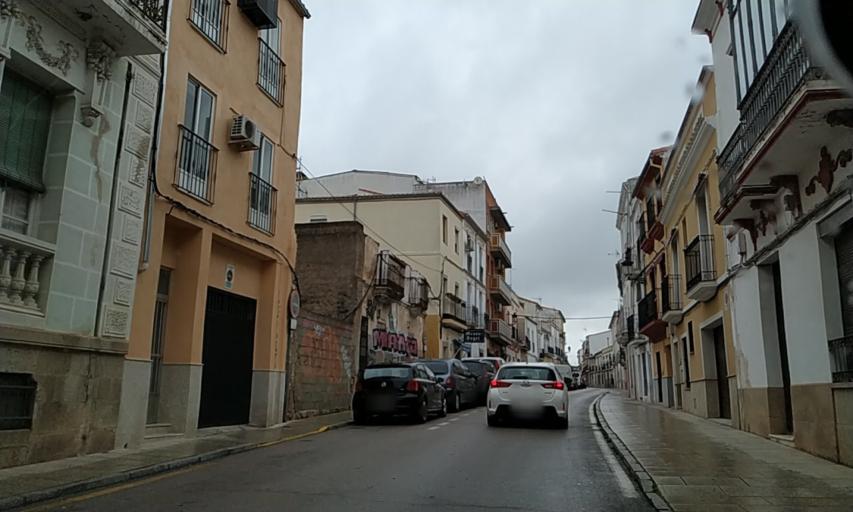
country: ES
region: Extremadura
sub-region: Provincia de Caceres
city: Caceres
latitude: 39.4776
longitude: -6.3731
